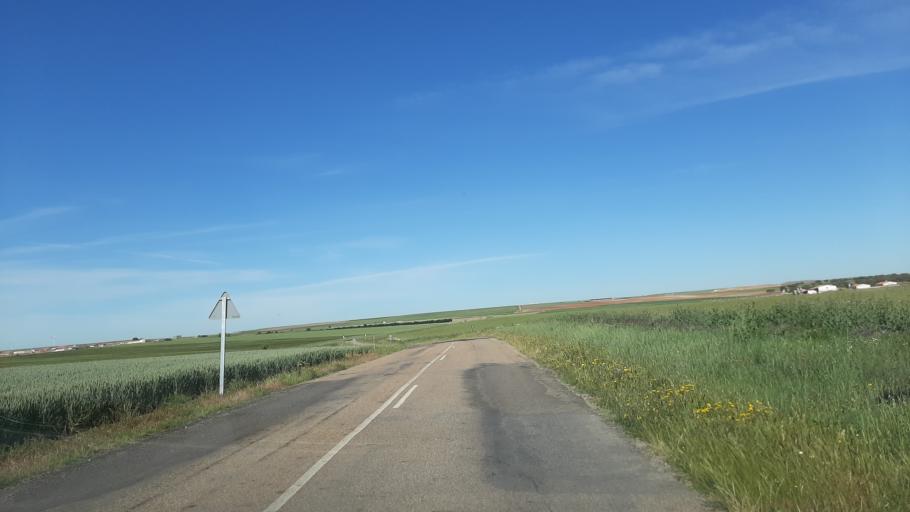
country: ES
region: Castille and Leon
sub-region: Provincia de Salamanca
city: Aldeaseca de Alba
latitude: 40.8252
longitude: -5.4292
